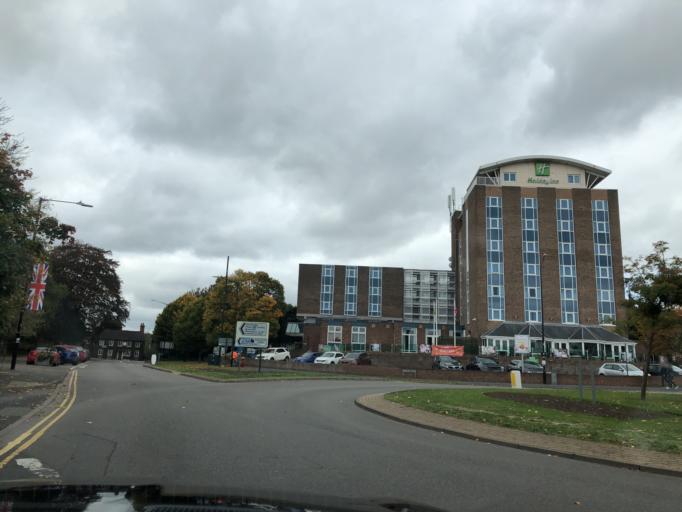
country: GB
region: England
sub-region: Warwickshire
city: Kenilworth
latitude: 52.3433
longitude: -1.5800
